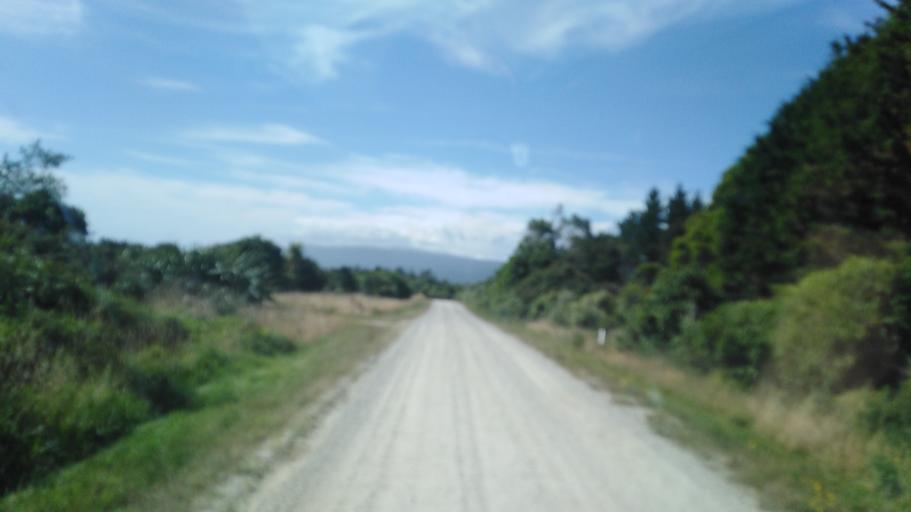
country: NZ
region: West Coast
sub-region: Buller District
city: Westport
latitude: -41.2635
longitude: 172.1141
